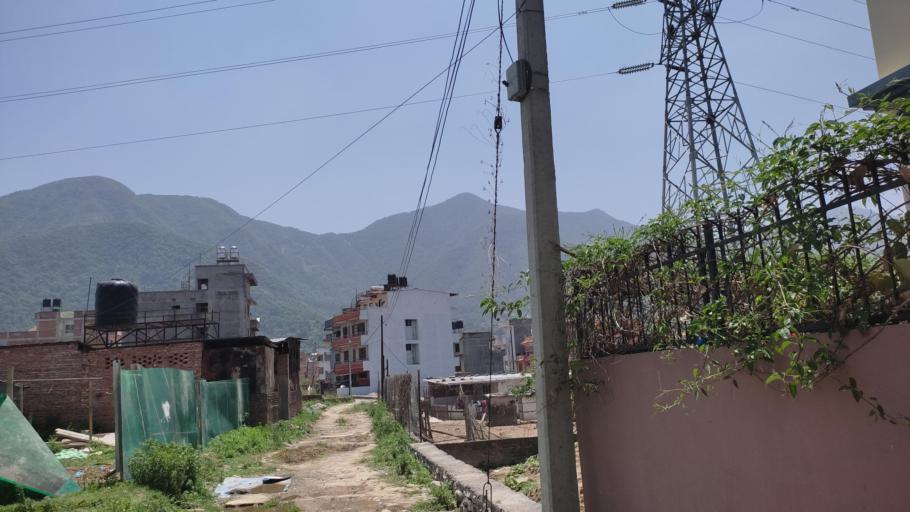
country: NP
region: Central Region
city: Kirtipur
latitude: 27.6690
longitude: 85.2682
